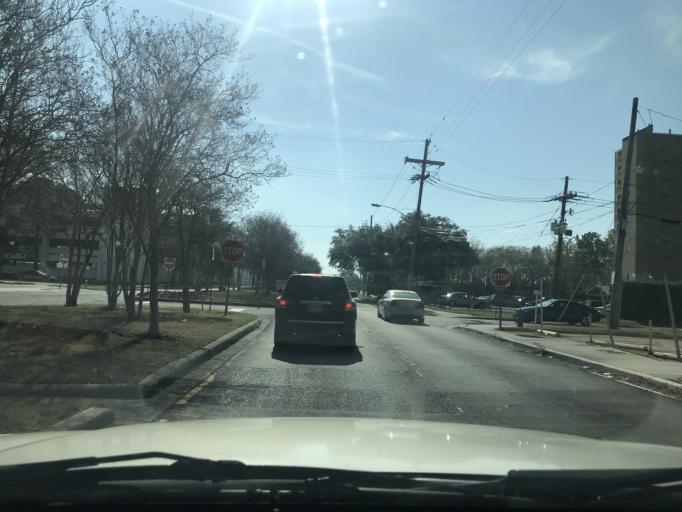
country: US
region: Louisiana
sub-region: Jefferson Parish
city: Marrero
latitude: 29.8937
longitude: -90.0963
